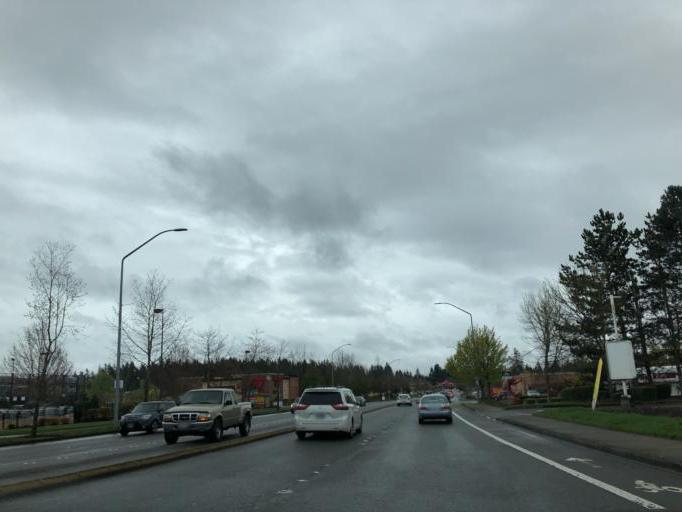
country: US
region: Washington
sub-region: Thurston County
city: Tanglewilde-Thompson Place
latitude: 47.0612
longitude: -122.7649
